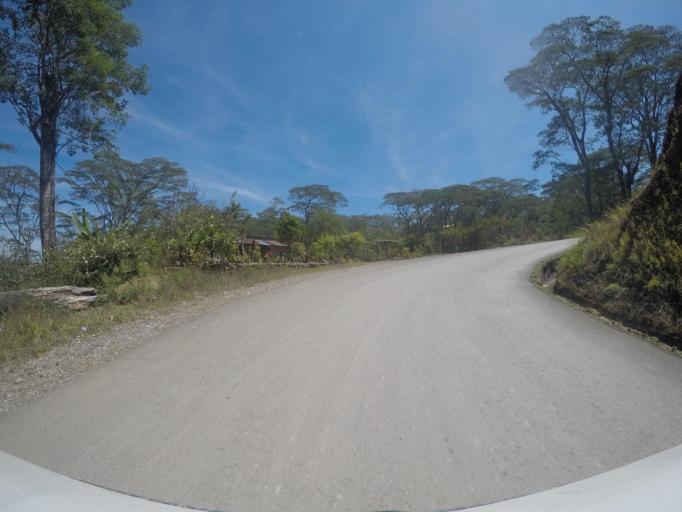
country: TL
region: Ermera
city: Gleno
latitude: -8.7883
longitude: 125.3782
